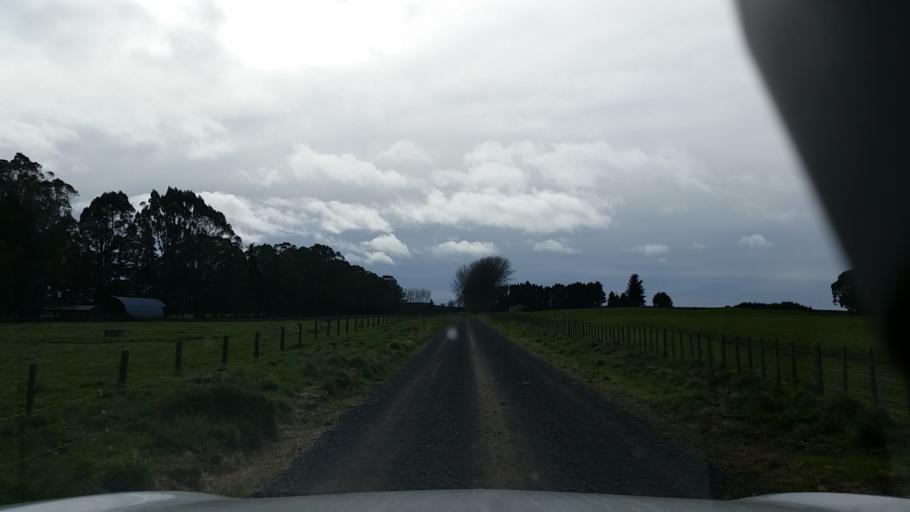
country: NZ
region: Bay of Plenty
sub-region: Whakatane District
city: Murupara
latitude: -38.4765
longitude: 176.4153
